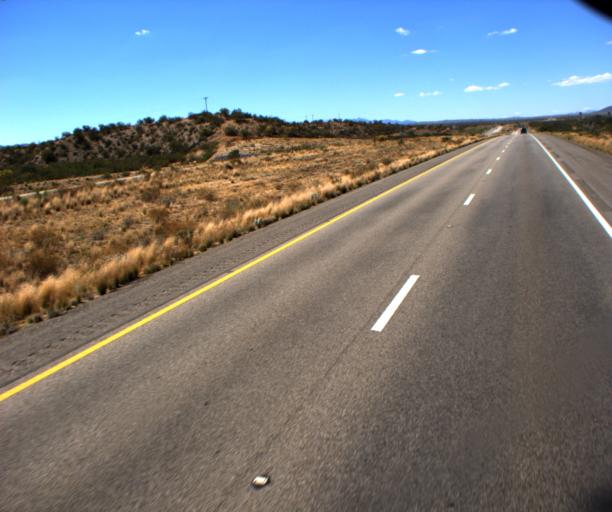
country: US
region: Arizona
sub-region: Yavapai County
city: Bagdad
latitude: 34.8260
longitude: -113.6283
